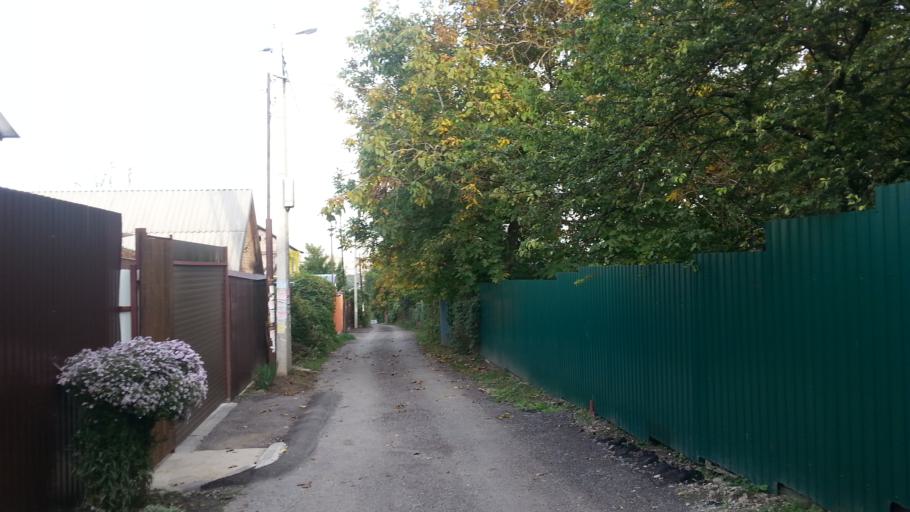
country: RU
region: Rostov
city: Severnyy
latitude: 47.2901
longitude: 39.6704
